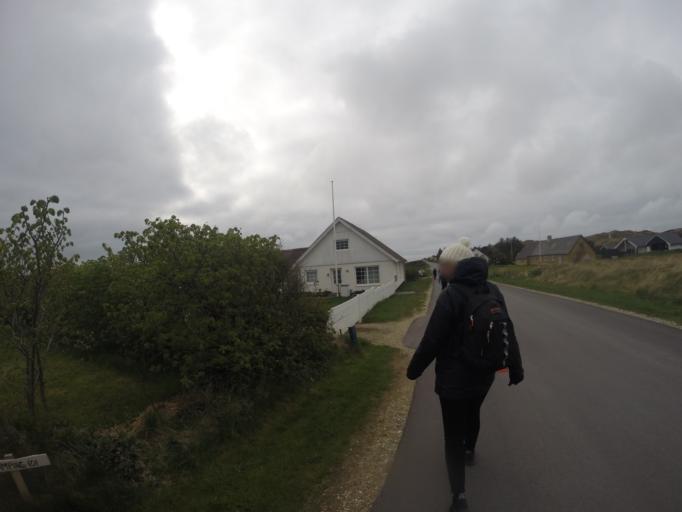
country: DK
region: North Denmark
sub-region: Thisted Kommune
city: Hurup
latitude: 56.9229
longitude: 8.3542
